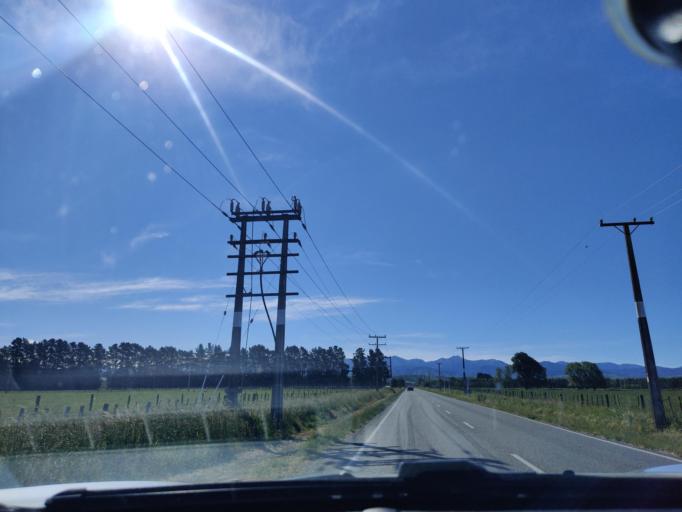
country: NZ
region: Wellington
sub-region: Masterton District
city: Masterton
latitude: -40.9359
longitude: 175.6511
